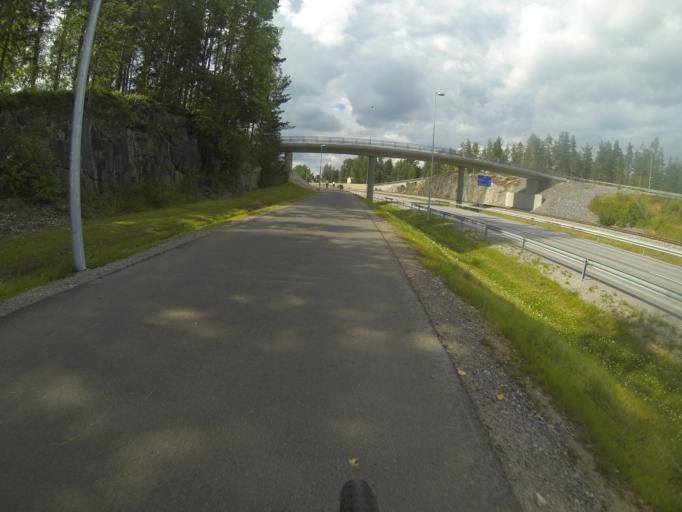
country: FI
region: Southern Savonia
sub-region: Savonlinna
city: Savonlinna
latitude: 61.8785
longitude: 28.8719
